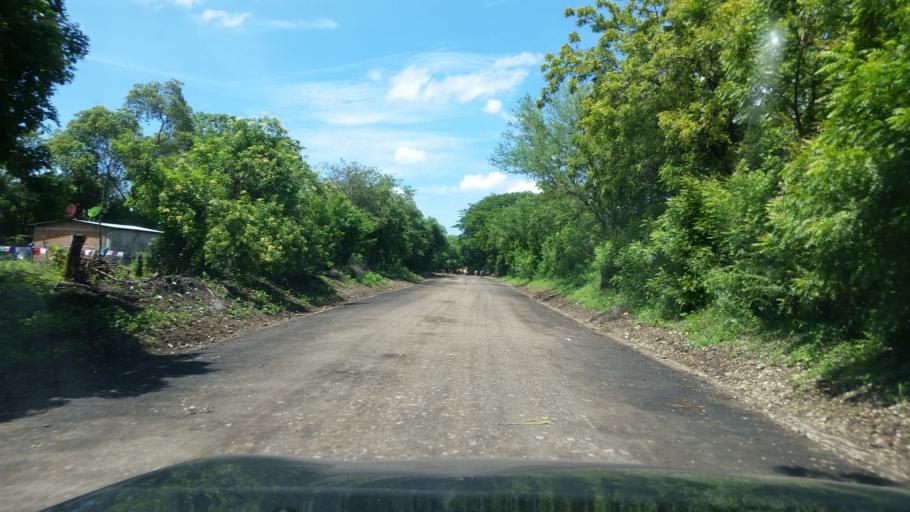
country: NI
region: Chinandega
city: El Viejo
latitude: 12.7473
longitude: -87.1340
